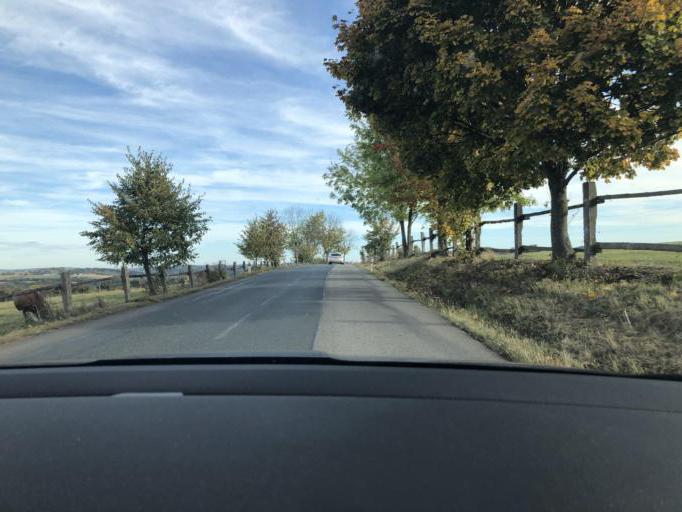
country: CZ
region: Central Bohemia
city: Divisov
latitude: 49.8026
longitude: 14.9162
